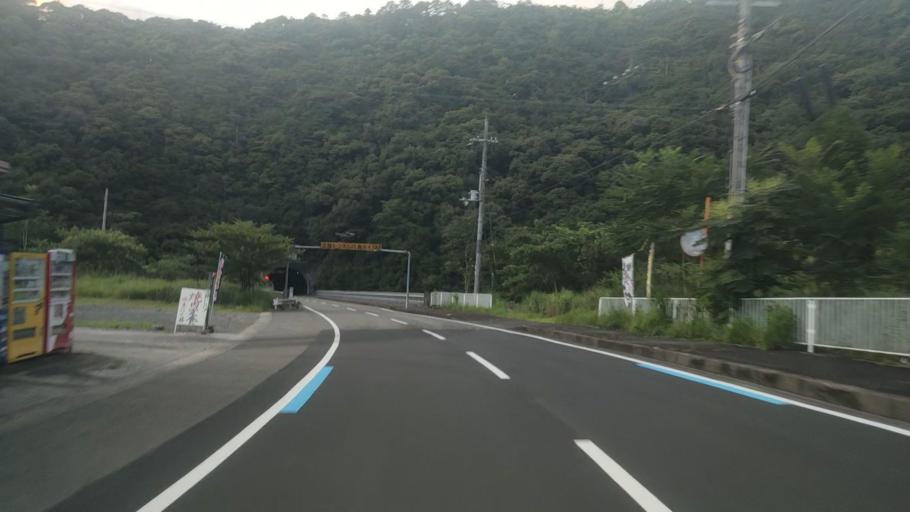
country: JP
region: Wakayama
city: Shingu
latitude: 33.8235
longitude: 135.7764
